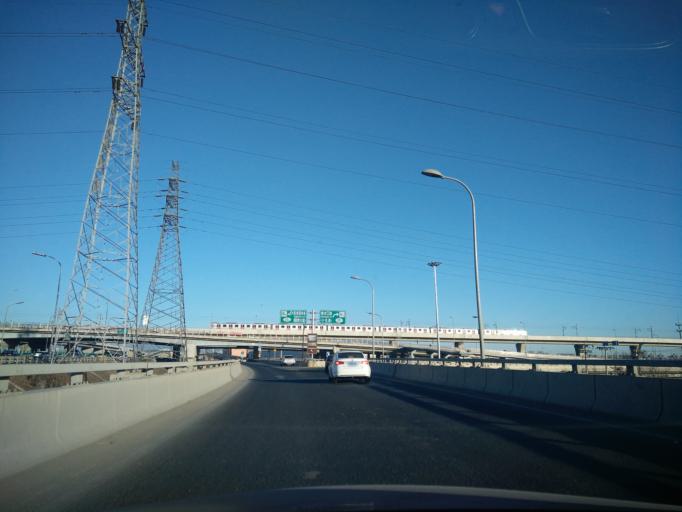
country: CN
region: Beijing
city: Lugu
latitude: 39.8623
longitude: 116.2100
